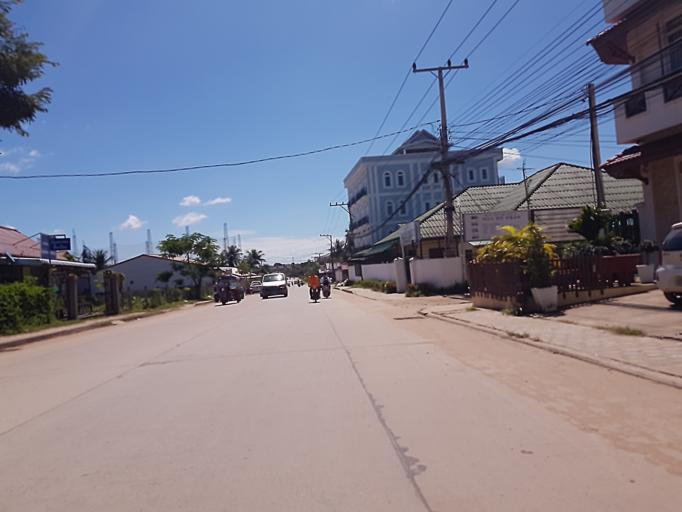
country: LA
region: Vientiane
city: Vientiane
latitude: 17.9428
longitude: 102.6313
